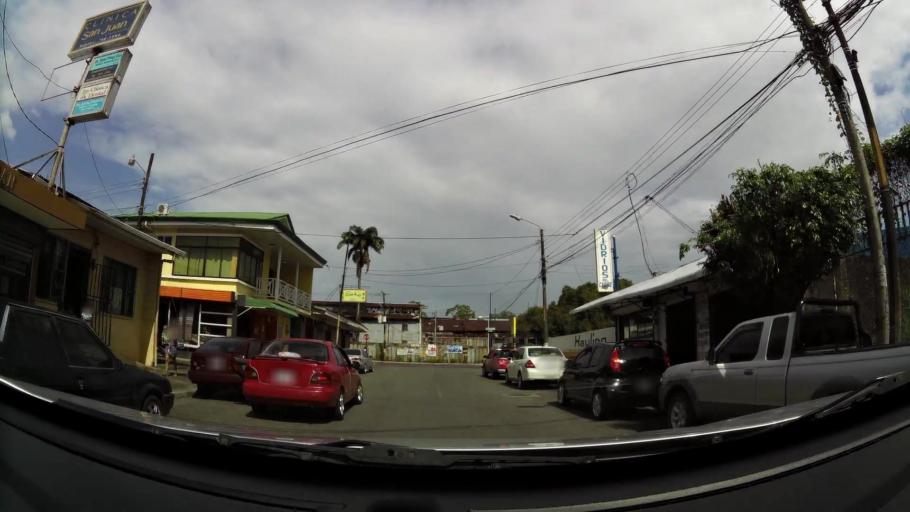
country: CR
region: Limon
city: Limon
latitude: 9.9956
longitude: -83.0290
